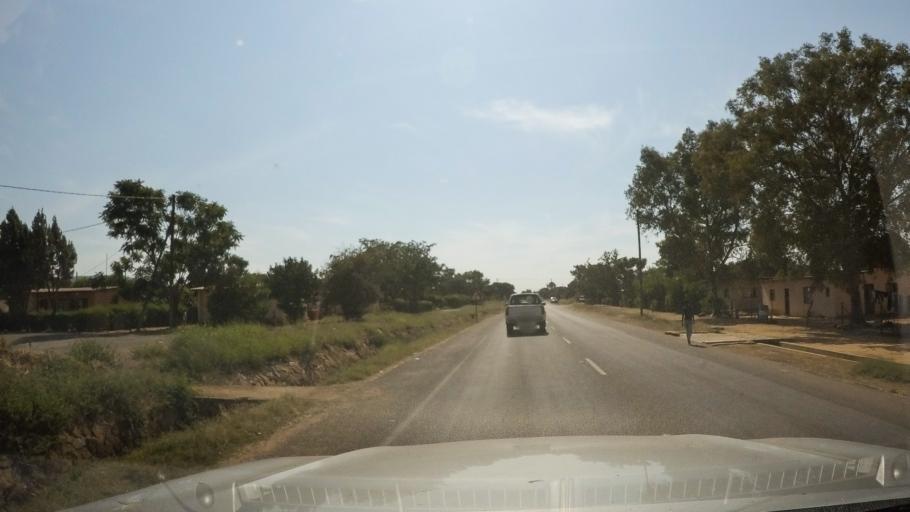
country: BW
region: South East
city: Lobatse
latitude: -25.2089
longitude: 25.6833
